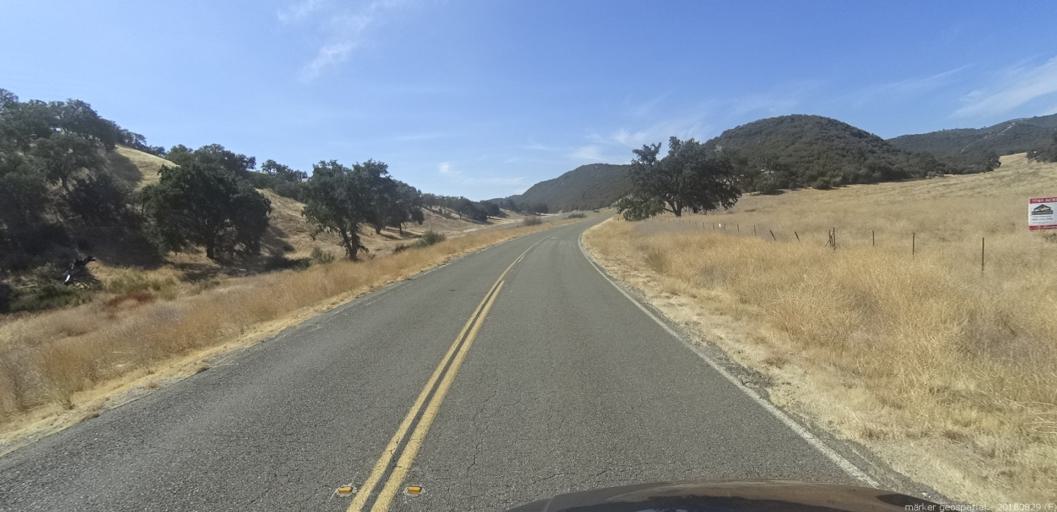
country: US
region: California
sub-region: San Luis Obispo County
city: Lake Nacimiento
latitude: 35.8836
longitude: -121.0656
